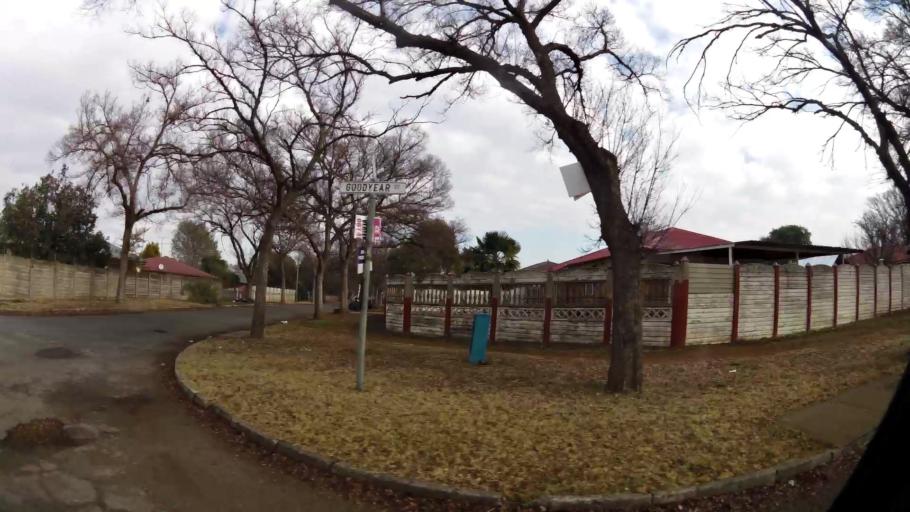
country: ZA
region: Gauteng
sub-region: Sedibeng District Municipality
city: Vanderbijlpark
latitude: -26.6945
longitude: 27.8142
